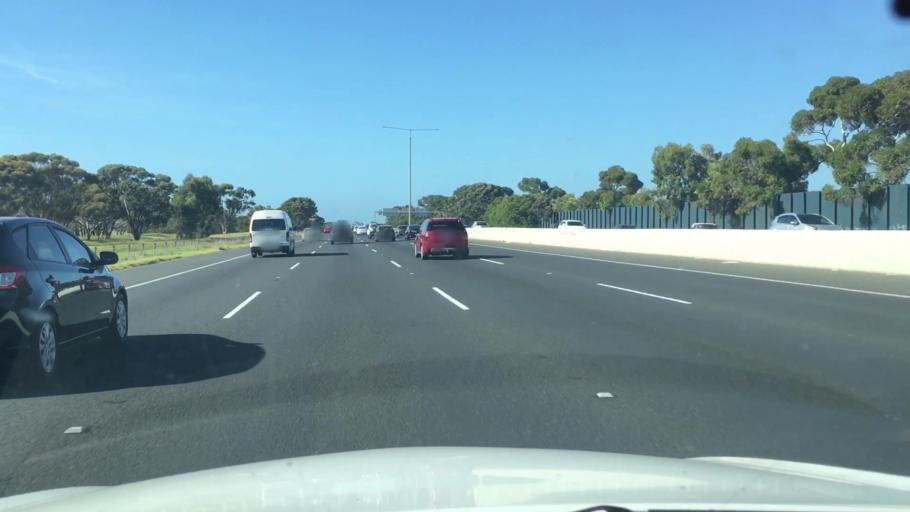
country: AU
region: Victoria
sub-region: Hobsons Bay
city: Laverton
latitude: -37.8416
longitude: 144.7808
